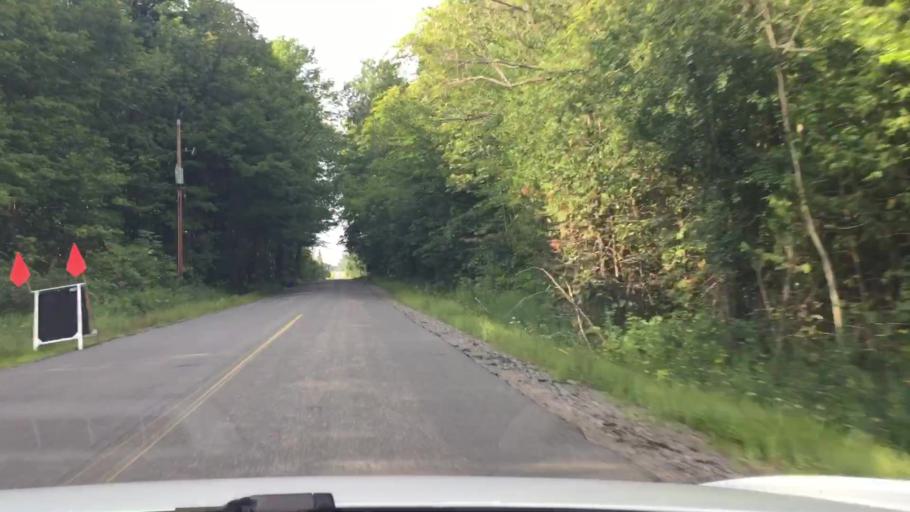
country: CA
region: Ontario
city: Oshawa
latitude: 43.9454
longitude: -78.7501
